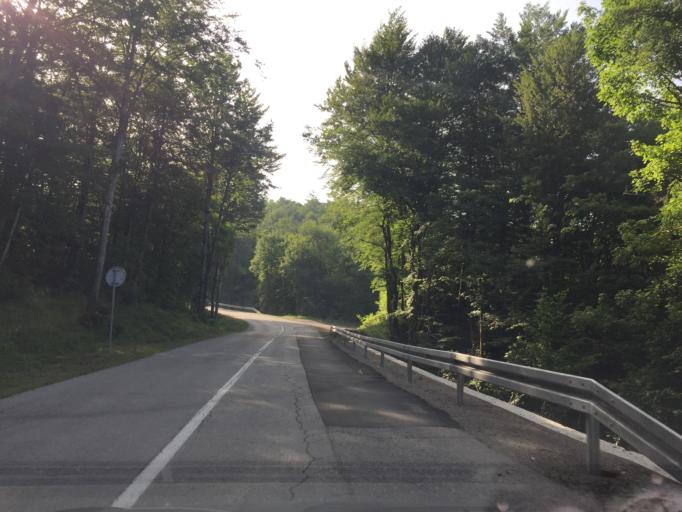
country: HR
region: Primorsko-Goranska
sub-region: Grad Opatija
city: Opatija
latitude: 45.4247
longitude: 14.2143
